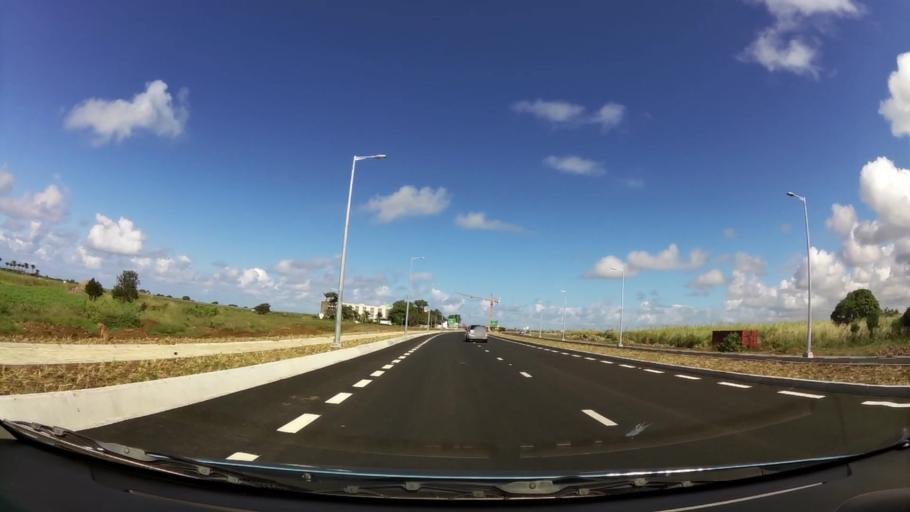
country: MU
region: Grand Port
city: Plaine Magnien
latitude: -20.4370
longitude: 57.6726
